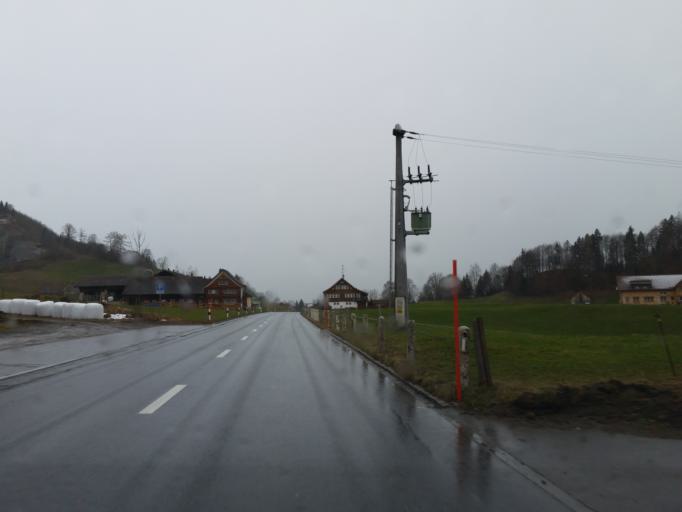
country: CH
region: Appenzell Innerrhoden
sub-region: Appenzell Inner Rhodes
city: Appenzell
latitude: 47.3424
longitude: 9.3881
